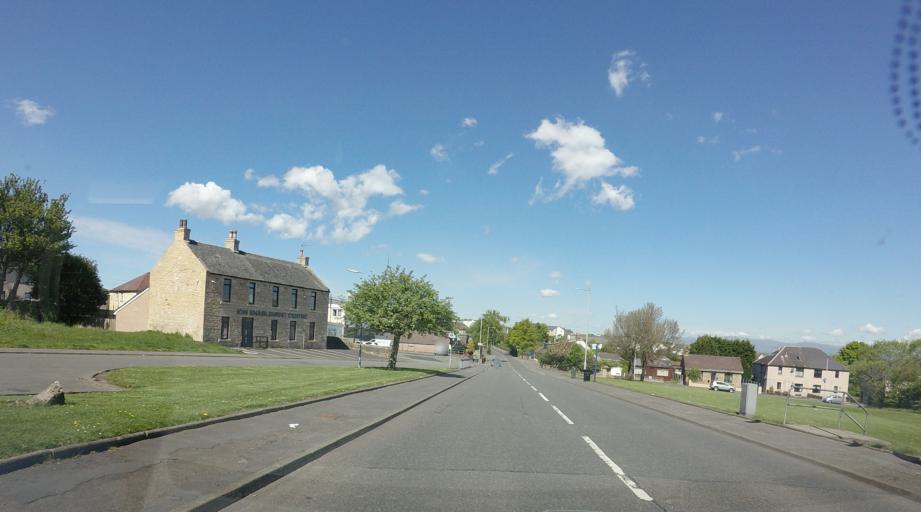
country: GB
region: Scotland
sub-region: Falkirk
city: Polmont
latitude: 55.9698
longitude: -3.6976
